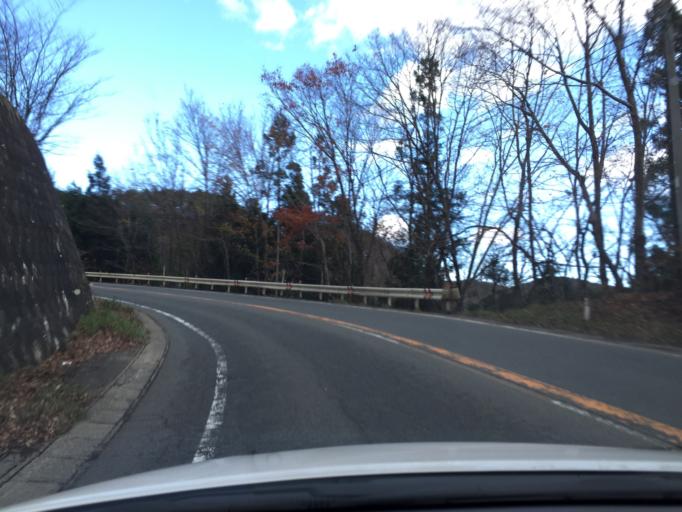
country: JP
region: Miyagi
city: Marumori
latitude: 37.6886
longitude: 140.8229
